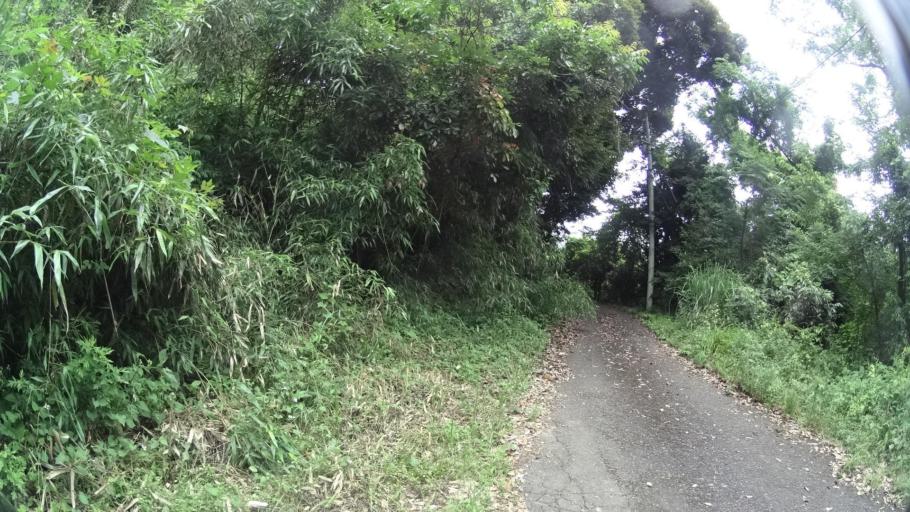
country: JP
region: Kyoto
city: Maizuru
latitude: 35.5335
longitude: 135.3424
